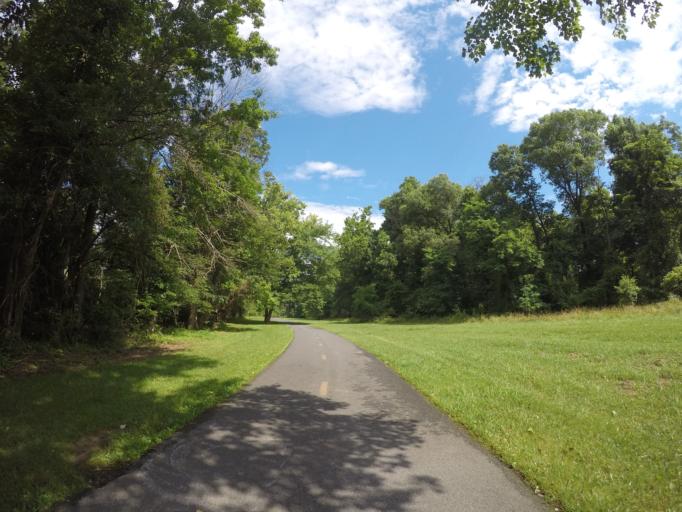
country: US
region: Maryland
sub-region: Prince George's County
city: East Riverdale
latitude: 38.9735
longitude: -76.9199
